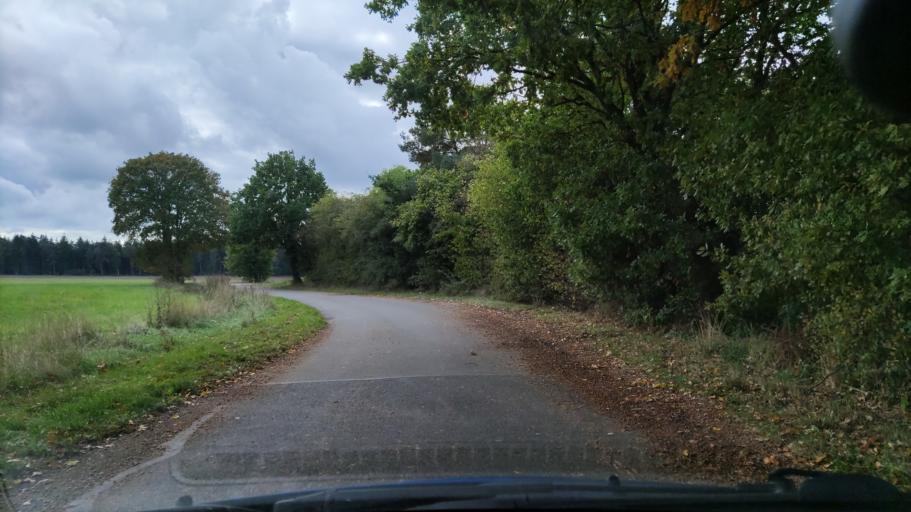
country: DE
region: Lower Saxony
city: Bienenbuttel
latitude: 53.1684
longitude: 10.5155
